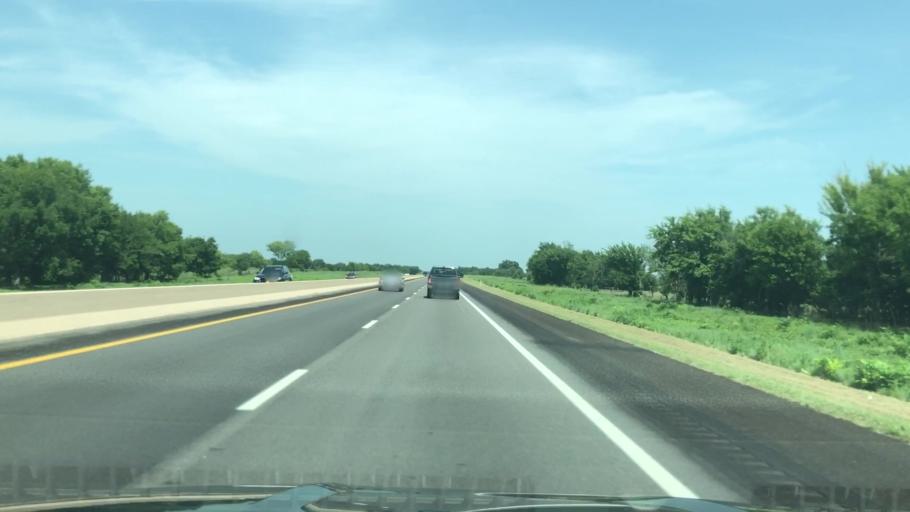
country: US
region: Oklahoma
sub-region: Craig County
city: Vinita
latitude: 36.6635
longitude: -95.0844
